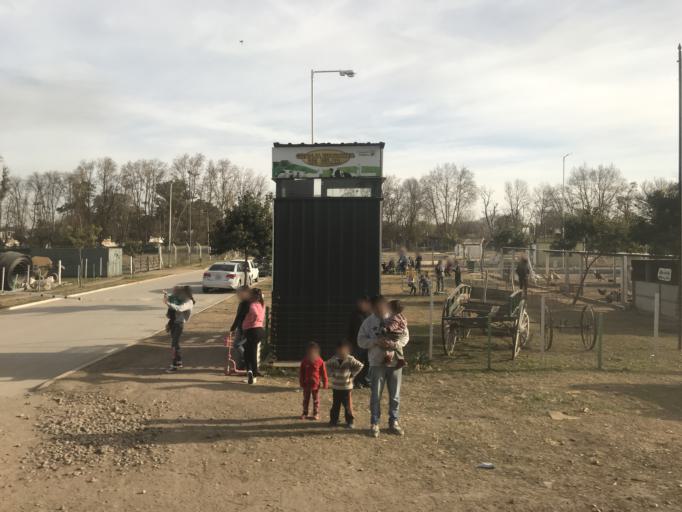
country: AR
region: Cordoba
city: Pilar
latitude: -31.6814
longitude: -63.8864
